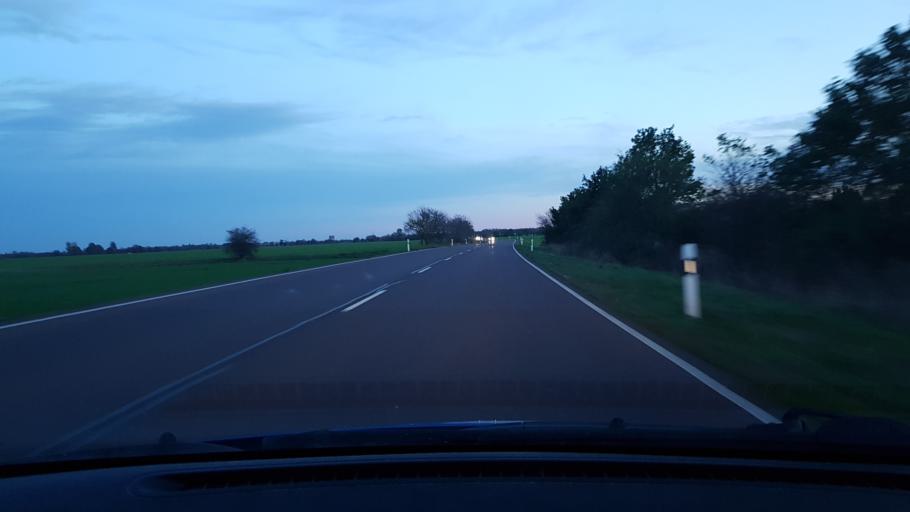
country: DE
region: Saxony-Anhalt
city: Zerbst
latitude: 51.9889
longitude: 12.0471
